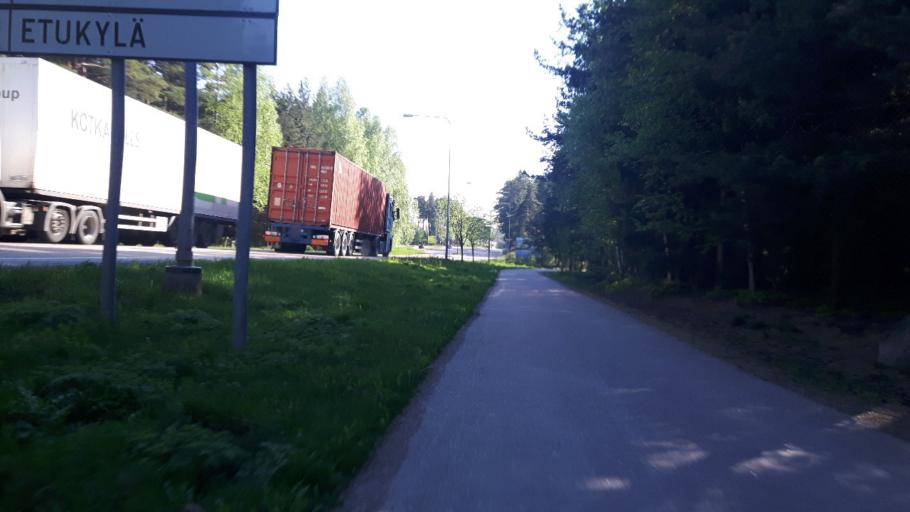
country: FI
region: Kymenlaakso
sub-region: Kotka-Hamina
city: Kotka
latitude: 60.4467
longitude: 26.8924
